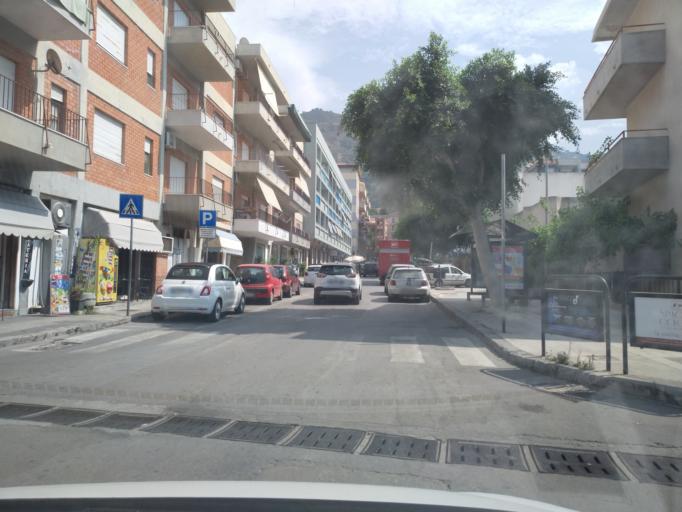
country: IT
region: Sicily
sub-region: Palermo
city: Cefalu
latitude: 38.0345
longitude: 14.0152
